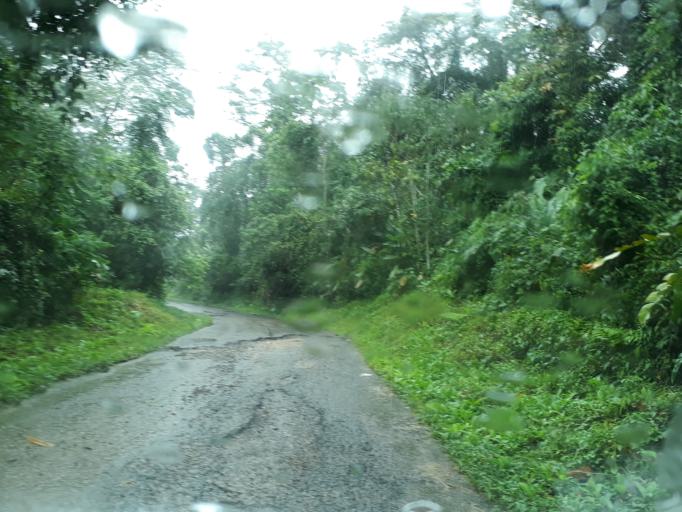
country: CO
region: Boyaca
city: Santa Maria
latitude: 4.7117
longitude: -73.2990
